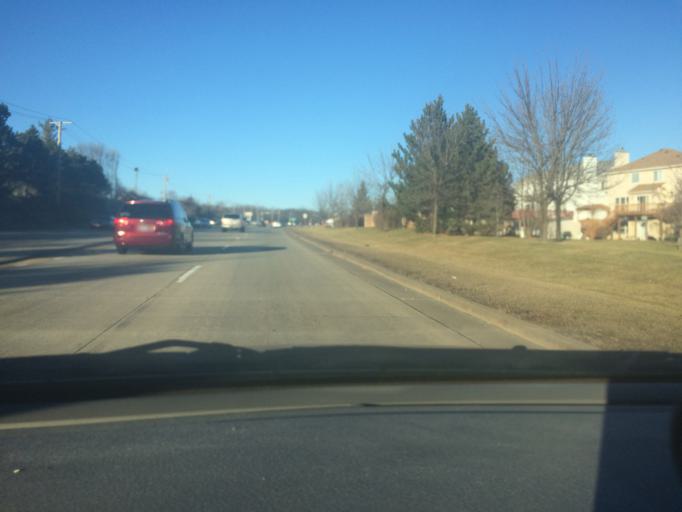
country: US
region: Illinois
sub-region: Cook County
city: Streamwood
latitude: 42.0282
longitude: -88.2026
